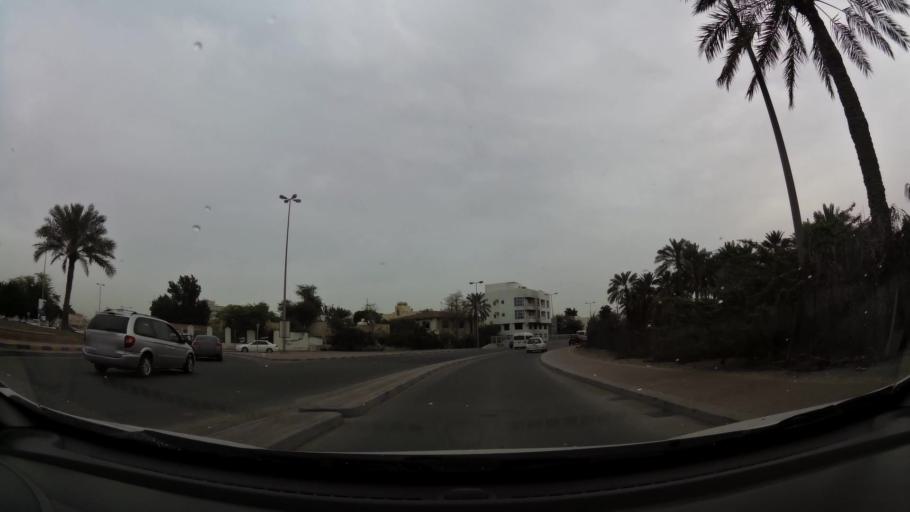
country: BH
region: Manama
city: Jidd Hafs
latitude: 26.2188
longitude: 50.5304
